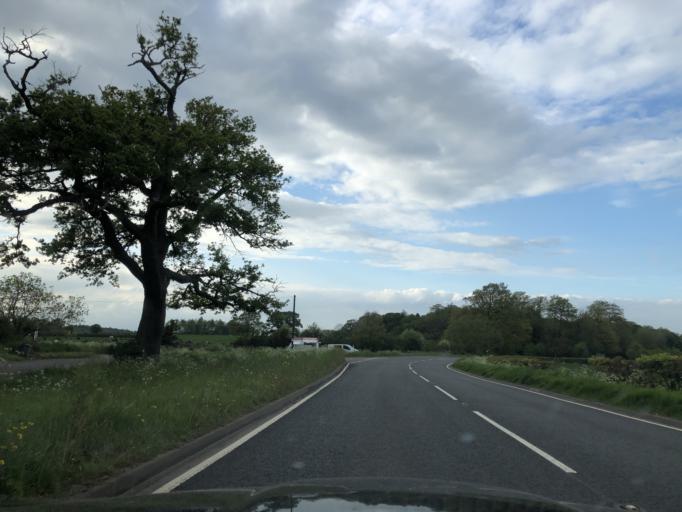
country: GB
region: England
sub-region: Gloucestershire
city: Moreton in Marsh
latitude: 52.0036
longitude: -1.6965
